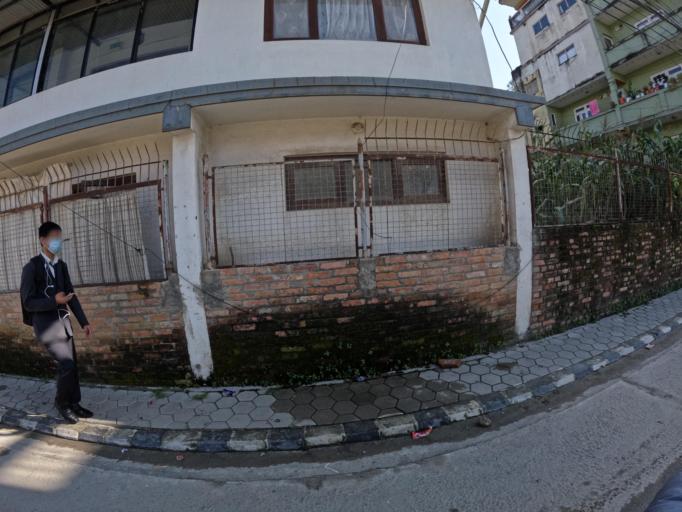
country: NP
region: Central Region
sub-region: Bagmati Zone
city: Kathmandu
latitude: 27.7527
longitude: 85.3345
